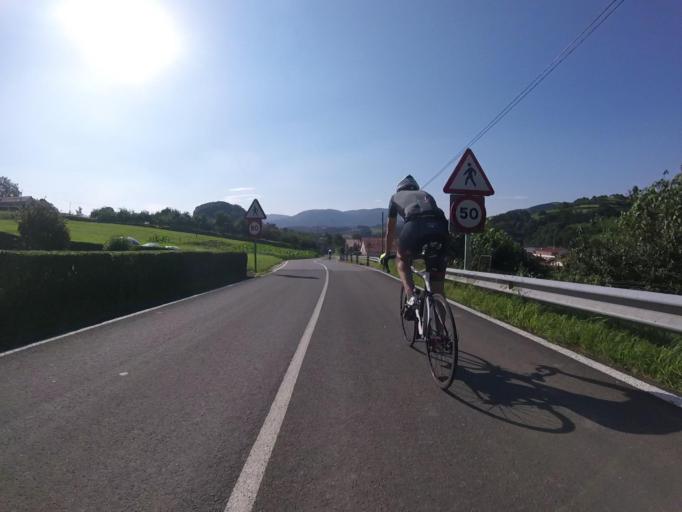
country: ES
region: Basque Country
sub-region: Provincia de Guipuzcoa
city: Asteasu
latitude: 43.1957
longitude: -2.0987
